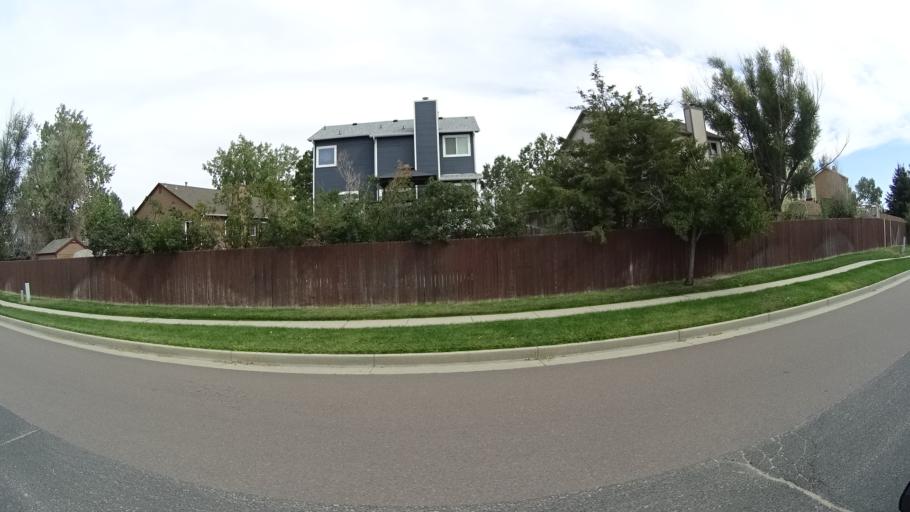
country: US
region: Colorado
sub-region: El Paso County
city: Cimarron Hills
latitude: 38.9024
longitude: -104.7023
